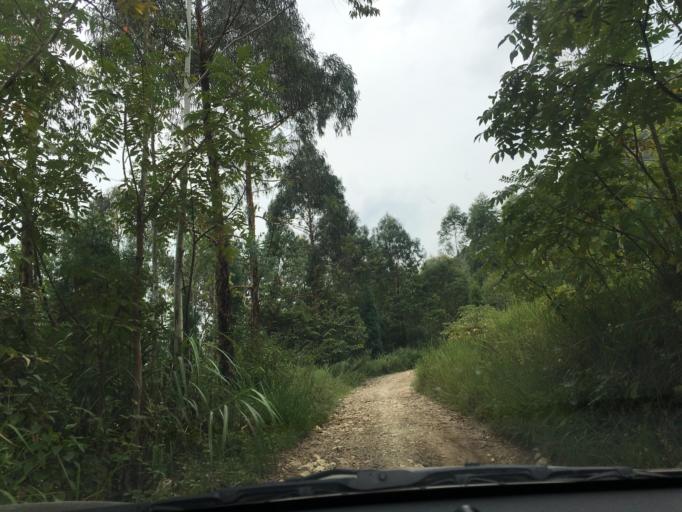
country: CN
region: Guangxi Zhuangzu Zizhiqu
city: Xinzhou
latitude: 25.3772
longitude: 105.6325
